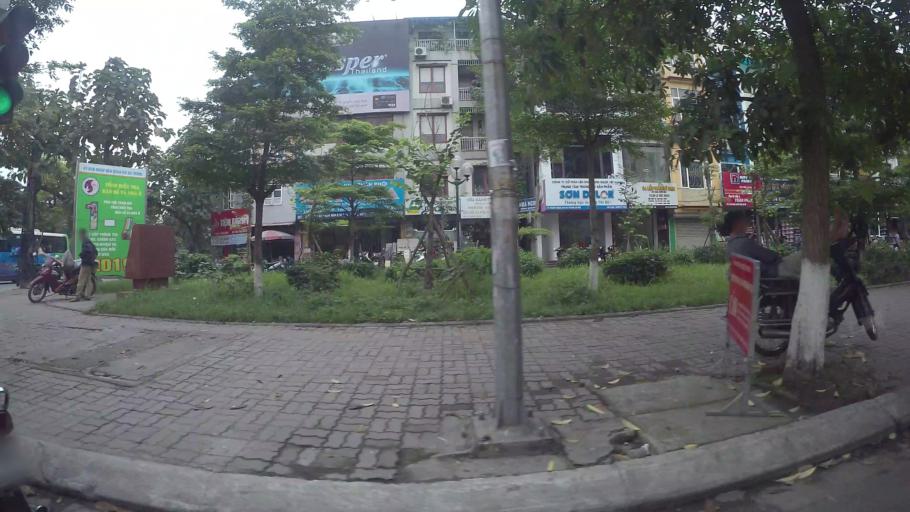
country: VN
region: Ha Noi
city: Hai BaTrung
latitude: 21.0029
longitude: 105.8611
